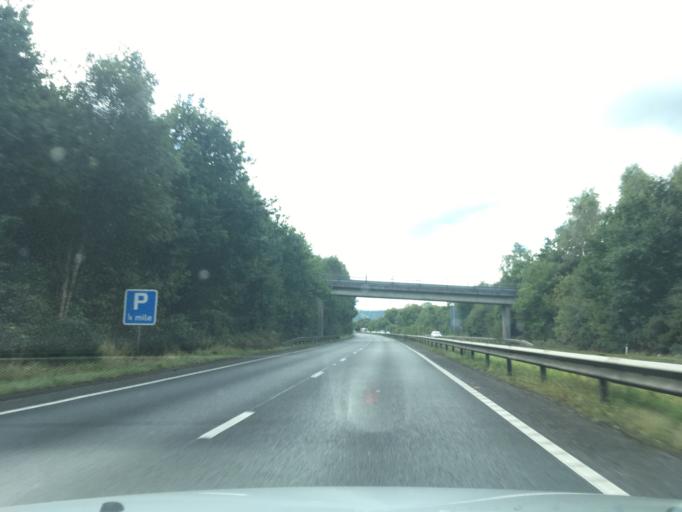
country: GB
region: England
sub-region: Hampshire
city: Liss
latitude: 51.0683
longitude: -0.8853
